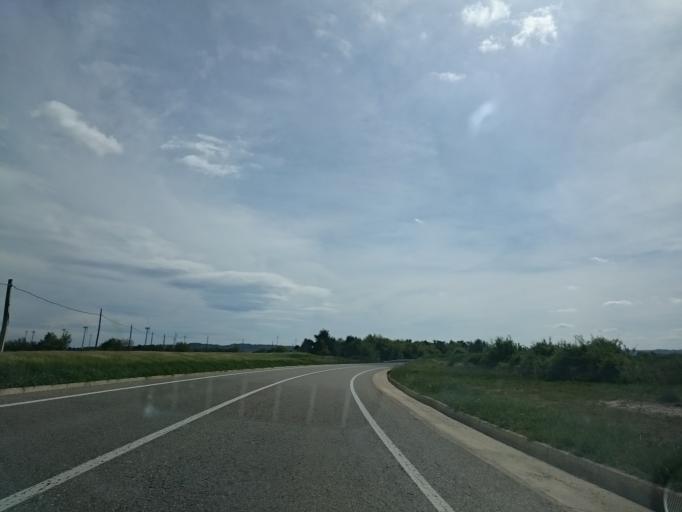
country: ES
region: Catalonia
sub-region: Provincia de Tarragona
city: Santa Coloma de Queralt
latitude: 41.5896
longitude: 1.3953
